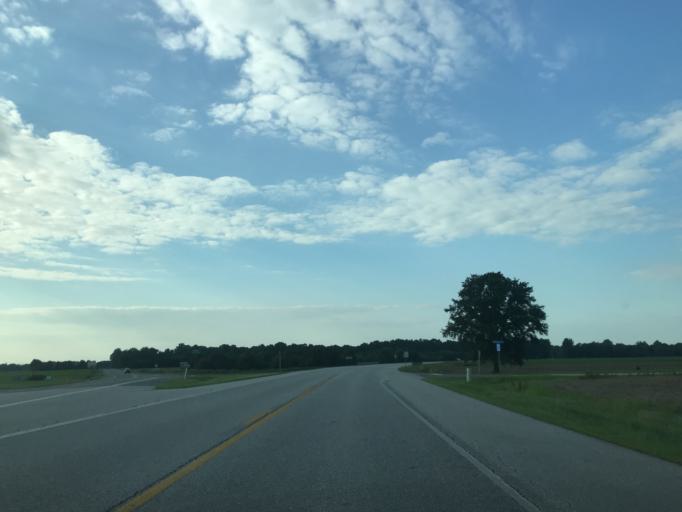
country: US
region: Maryland
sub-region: Caroline County
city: Federalsburg
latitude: 38.7458
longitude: -75.7939
